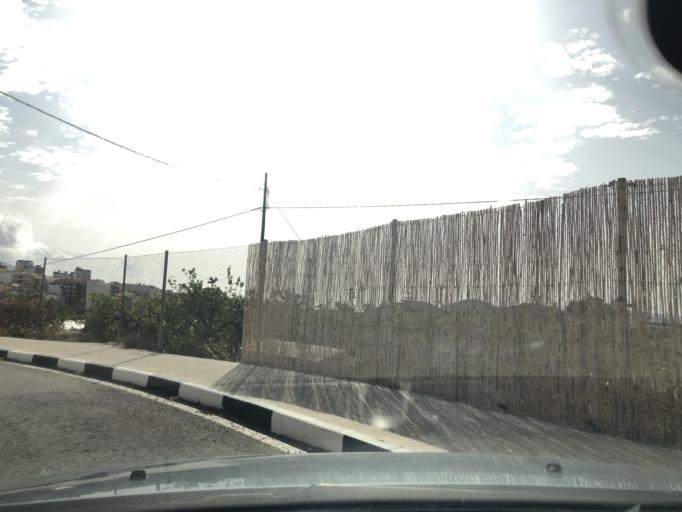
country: ES
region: Valencia
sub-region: Provincia de Alicante
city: Callosa d'En Sarria
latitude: 38.6511
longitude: -0.1301
